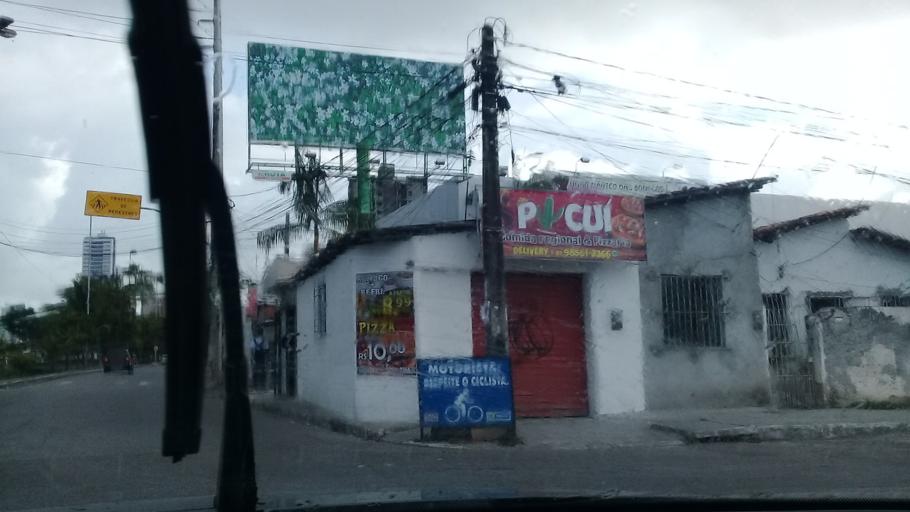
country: BR
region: Pernambuco
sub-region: Recife
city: Recife
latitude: -8.1250
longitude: -34.9100
